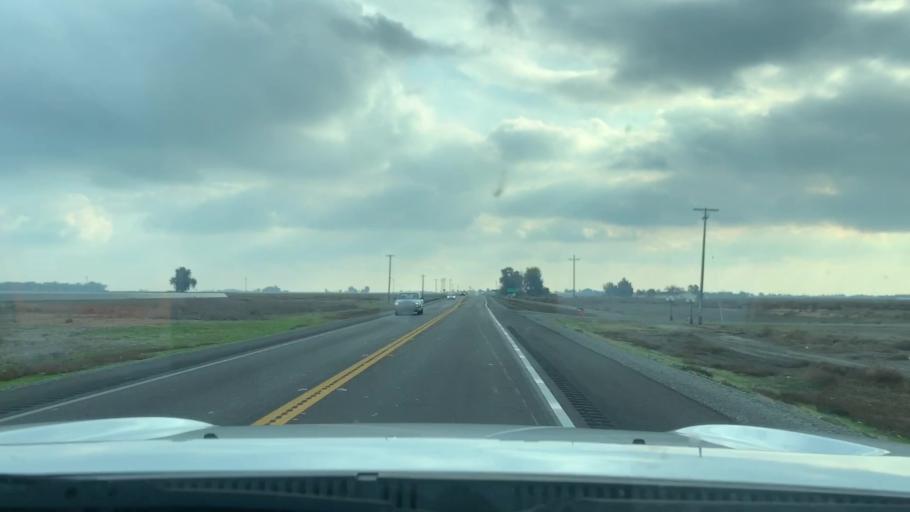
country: US
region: California
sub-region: Kings County
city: Stratford
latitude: 36.2161
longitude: -119.8162
